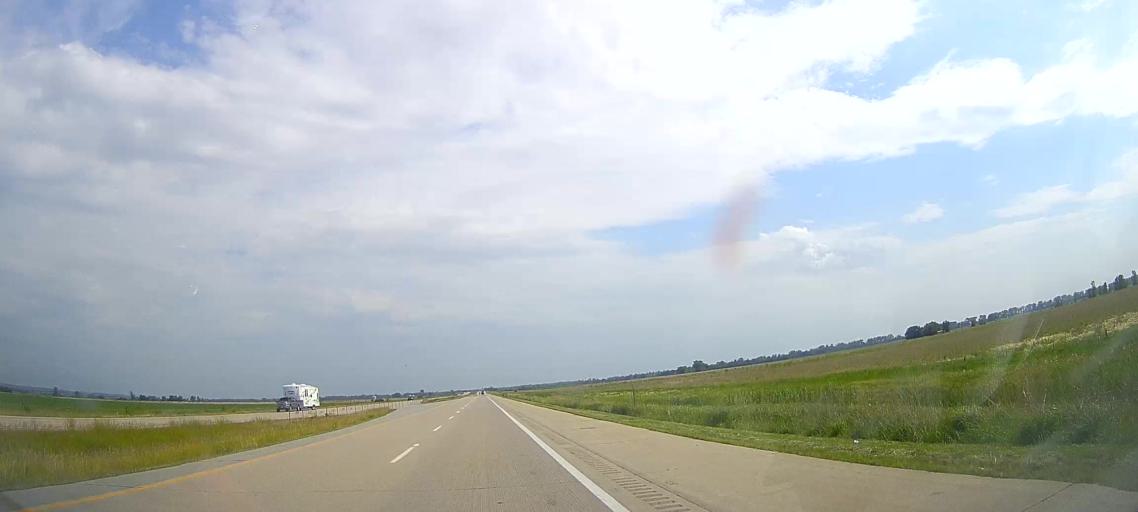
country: US
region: Iowa
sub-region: Monona County
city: Onawa
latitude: 41.8764
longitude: -96.1044
